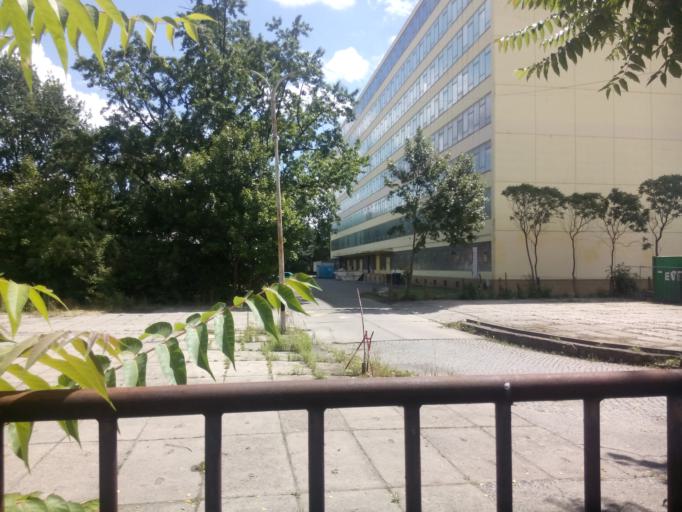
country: DE
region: Saxony
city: Albertstadt
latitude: 51.0459
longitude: 13.7832
